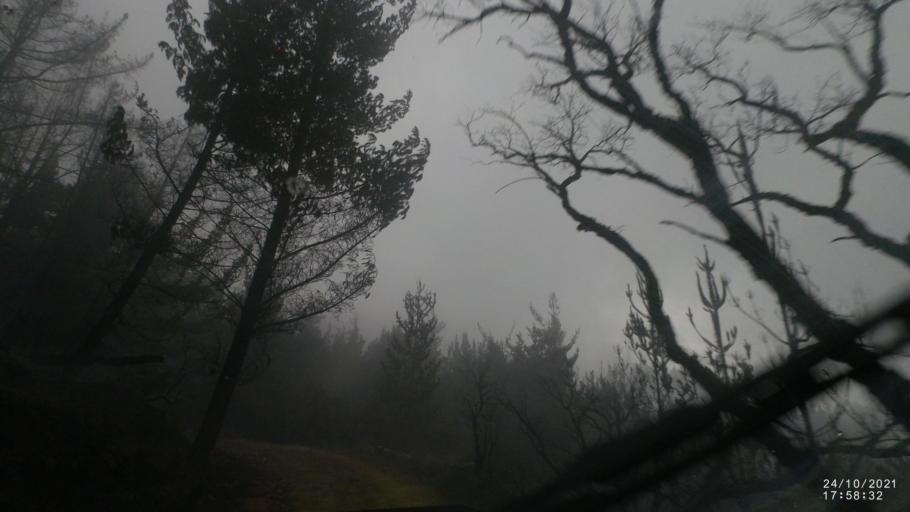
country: BO
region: Cochabamba
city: Cochabamba
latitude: -17.3249
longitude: -66.1297
